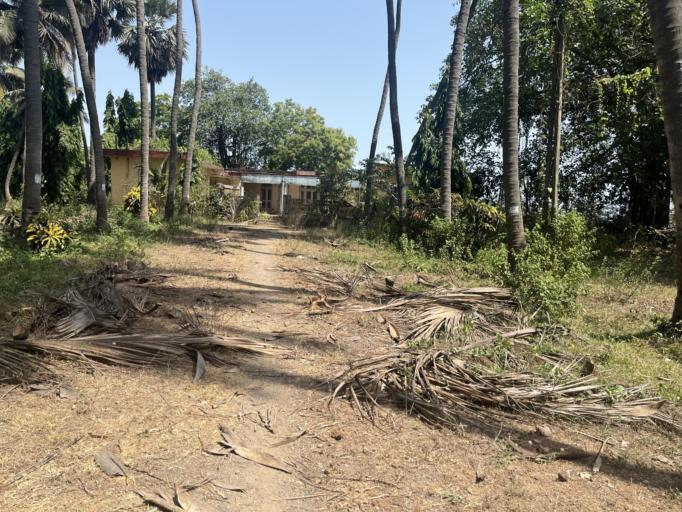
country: IN
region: Daman and Diu
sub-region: Daman District
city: Daman
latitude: 20.3515
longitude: 72.8092
